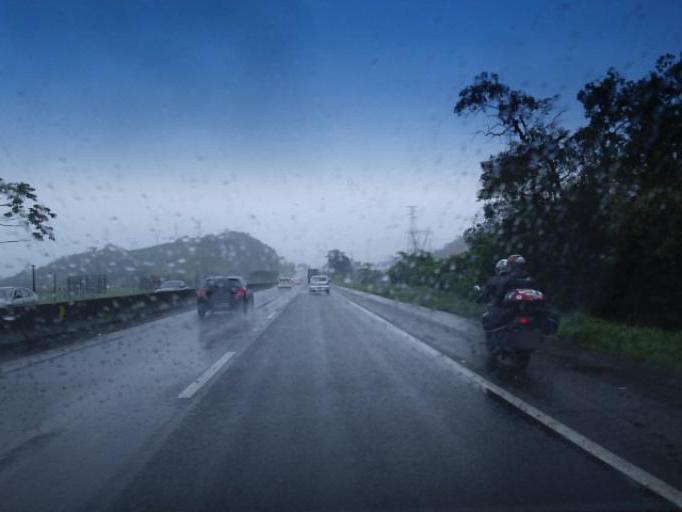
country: BR
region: Santa Catarina
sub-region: Joinville
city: Joinville
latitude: -26.1207
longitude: -48.8819
